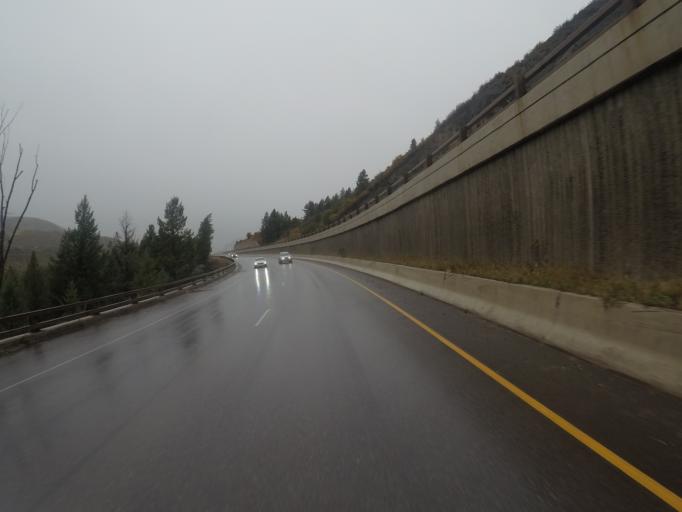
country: US
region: Colorado
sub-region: Pitkin County
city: Snowmass Village
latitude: 39.2436
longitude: -106.8810
